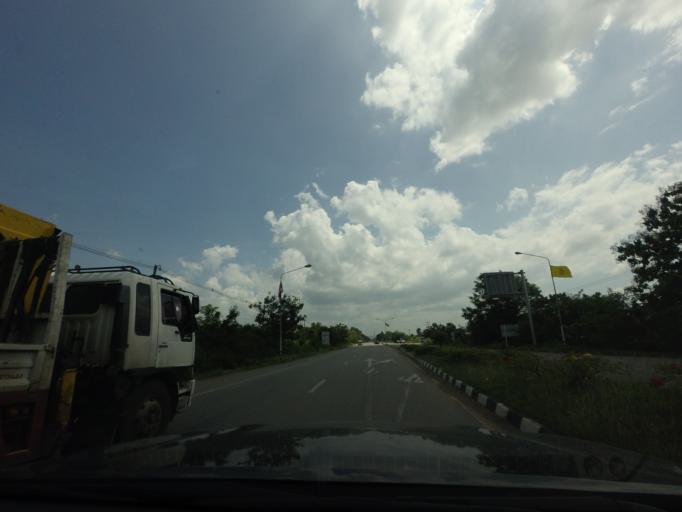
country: TH
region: Phetchabun
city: Phetchabun
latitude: 16.2471
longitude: 101.0717
